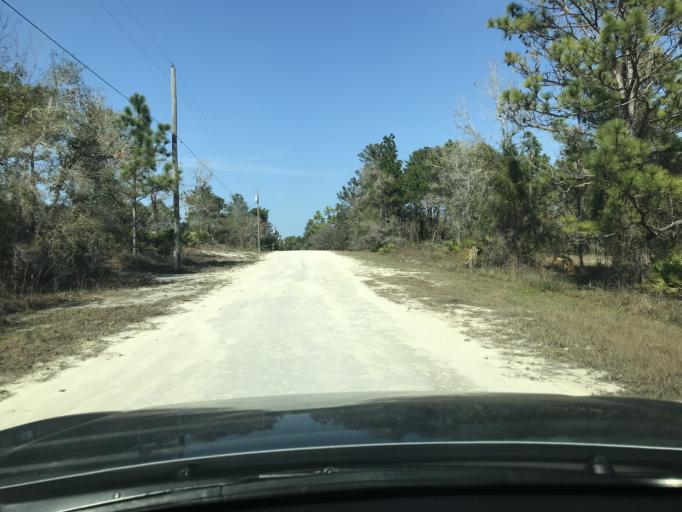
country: US
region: Florida
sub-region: Hernando County
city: North Weeki Wachee
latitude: 28.5486
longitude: -82.5511
